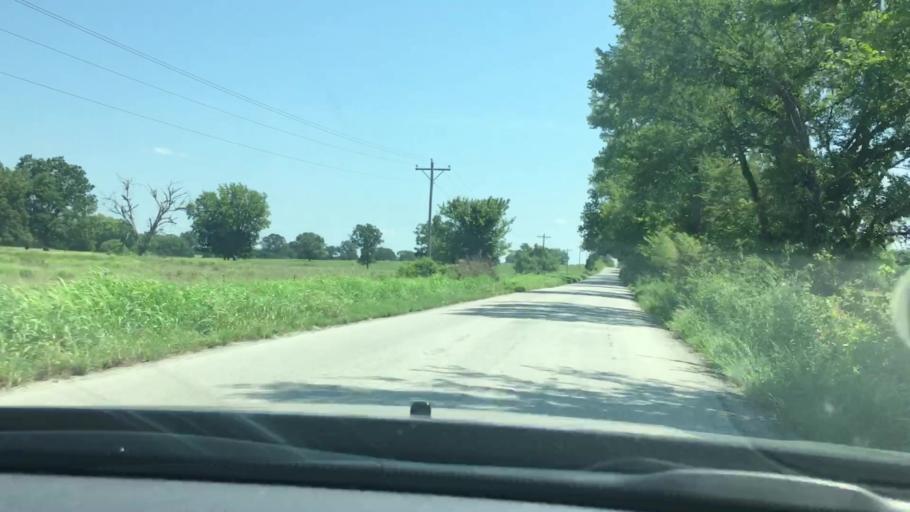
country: US
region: Oklahoma
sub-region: Bryan County
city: Durant
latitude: 34.2588
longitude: -96.3955
